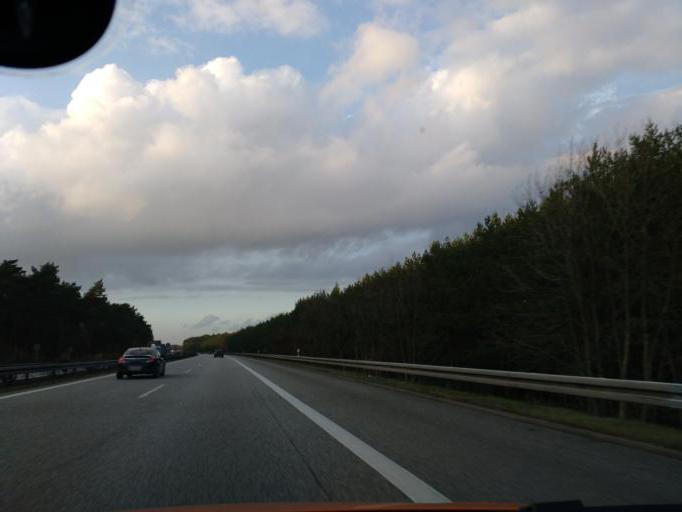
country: DE
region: Mecklenburg-Vorpommern
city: Neustadt-Glewe
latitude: 53.3863
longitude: 11.6120
